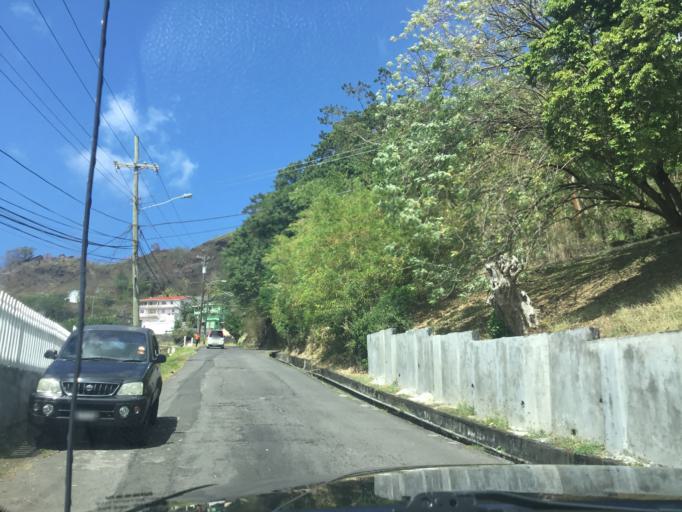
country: VC
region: Saint George
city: Kingstown Park
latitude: 13.1608
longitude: -61.2339
